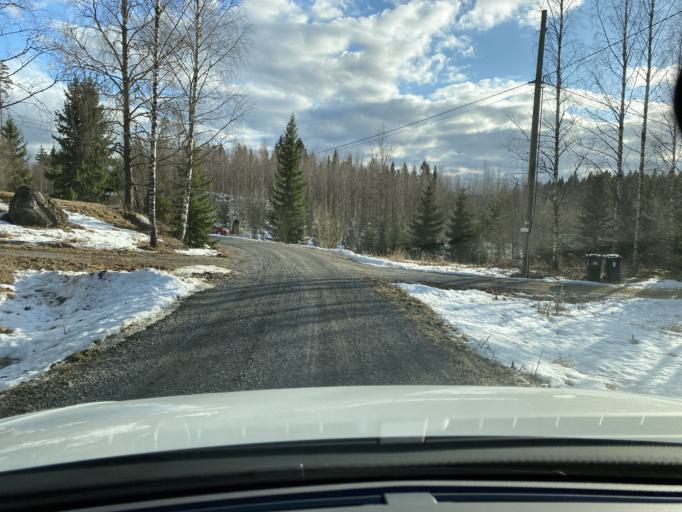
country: FI
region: Pirkanmaa
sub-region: Lounais-Pirkanmaa
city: Mouhijaervi
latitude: 61.4463
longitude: 22.9604
